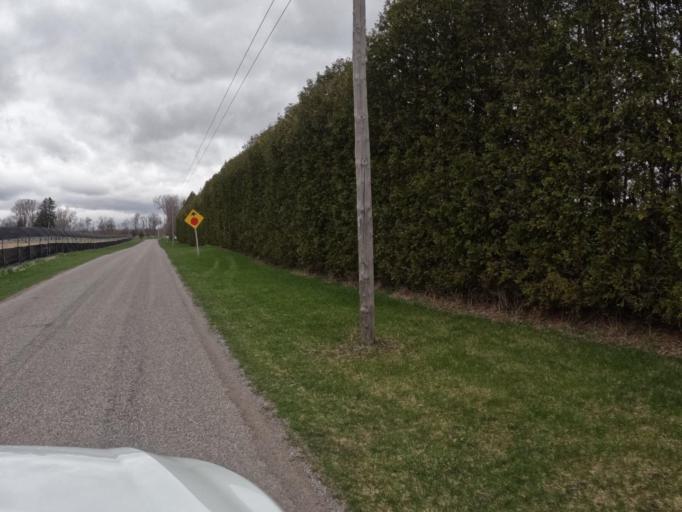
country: CA
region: Ontario
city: Norfolk County
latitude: 42.9623
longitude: -80.4276
